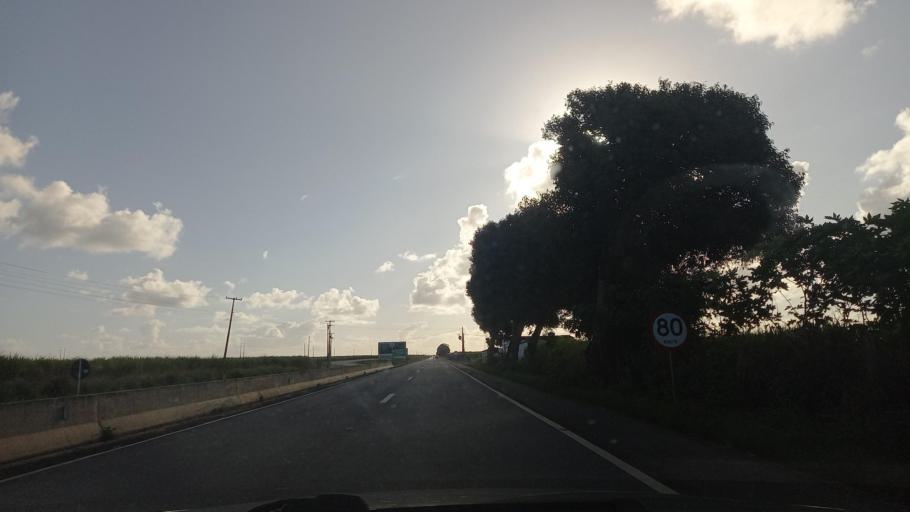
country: BR
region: Alagoas
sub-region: Sao Miguel Dos Campos
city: Sao Miguel dos Campos
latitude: -9.8043
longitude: -36.1335
